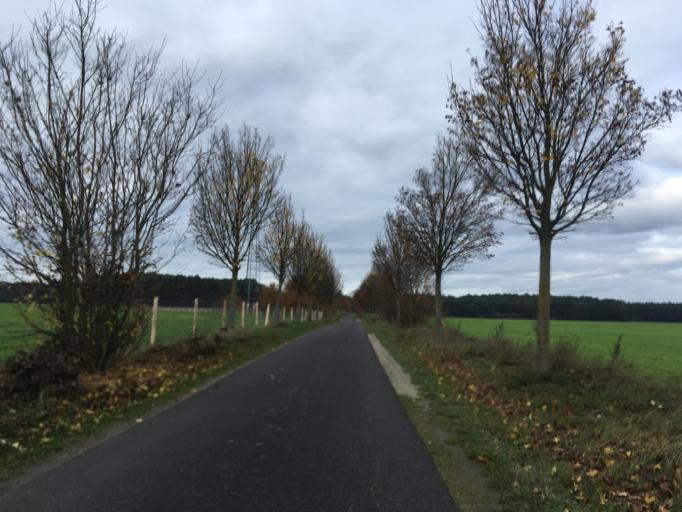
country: DE
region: Brandenburg
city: Schenkendobern
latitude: 51.9848
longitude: 14.5262
